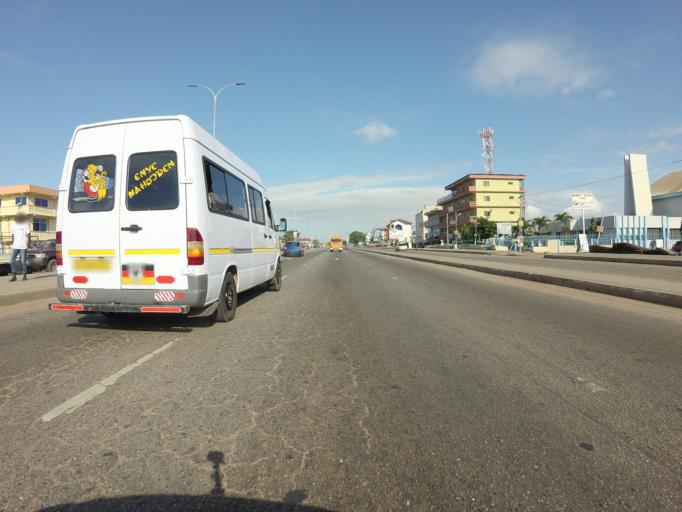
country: GH
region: Greater Accra
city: Gbawe
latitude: 5.5773
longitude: -0.2558
